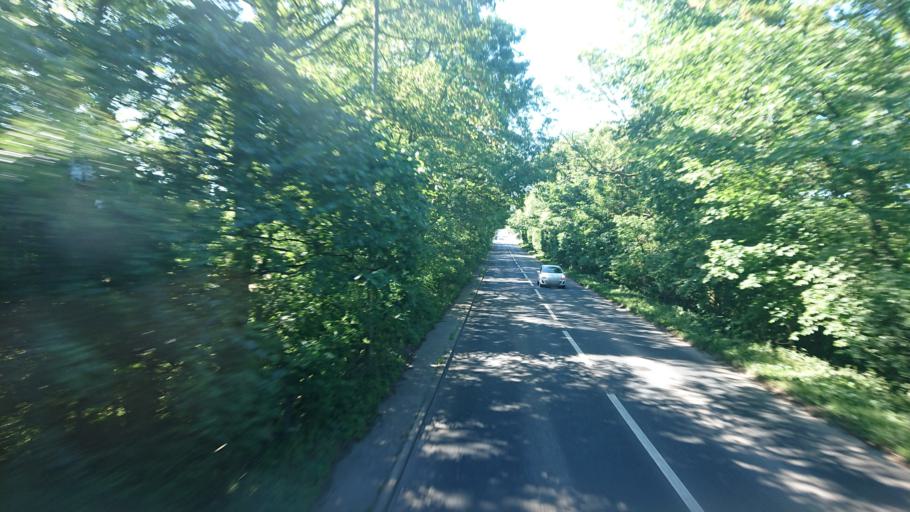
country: GB
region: England
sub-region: Lancashire
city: Bay Horse
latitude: 53.9695
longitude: -2.7812
